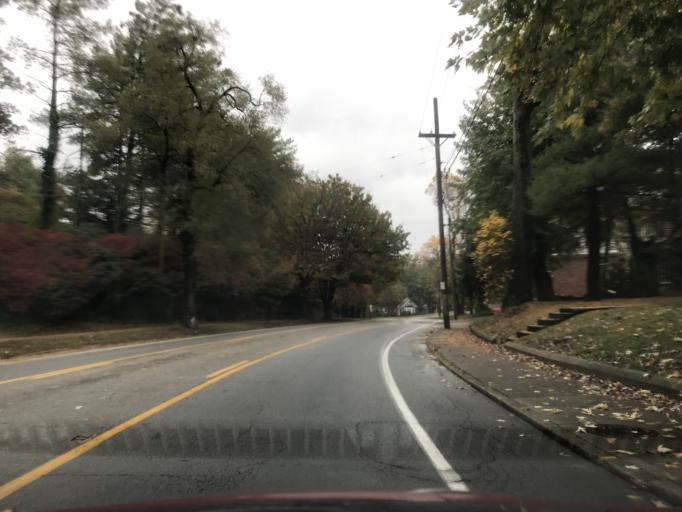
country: US
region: Kentucky
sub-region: Jefferson County
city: Audubon Park
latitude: 38.2433
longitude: -85.7088
